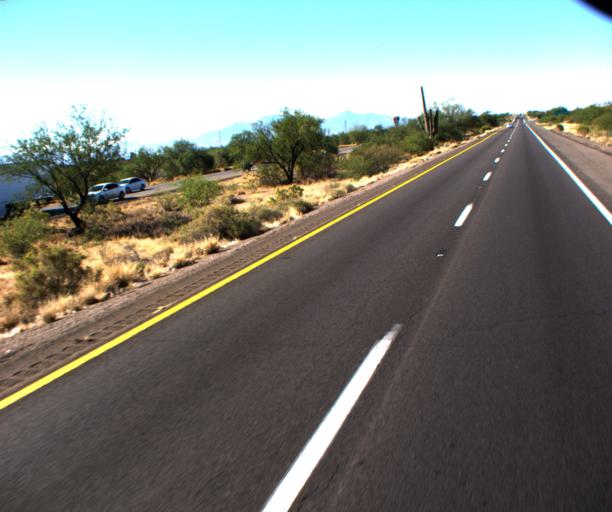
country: US
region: Arizona
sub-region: Pima County
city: Sahuarita
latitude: 32.0102
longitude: -110.9925
